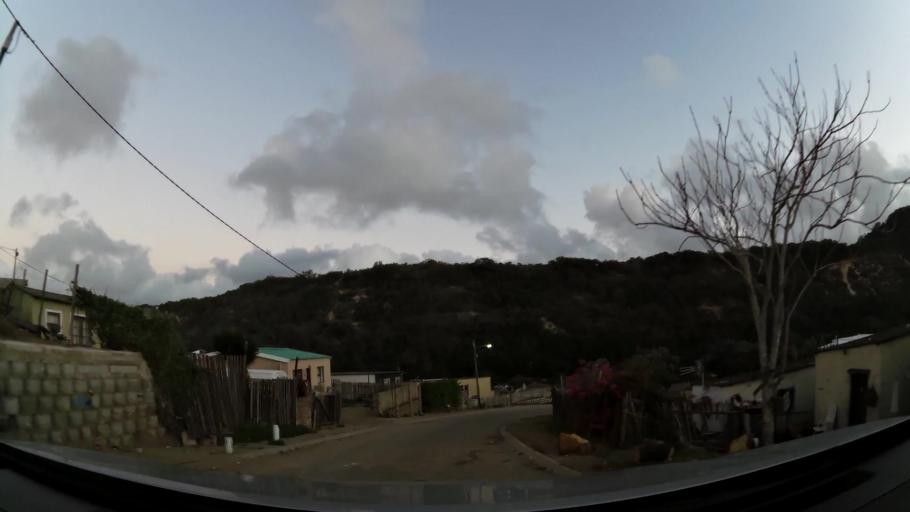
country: ZA
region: Western Cape
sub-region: Eden District Municipality
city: Knysna
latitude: -34.0270
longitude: 22.8213
